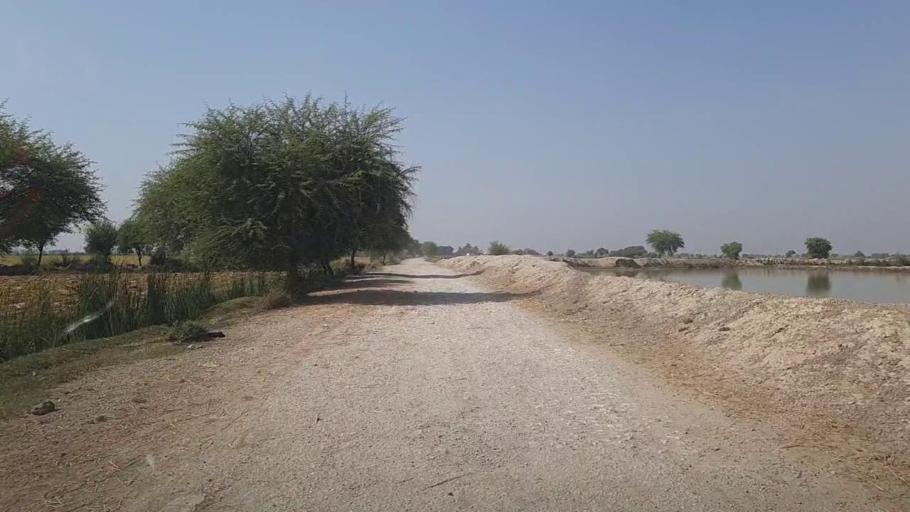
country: PK
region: Sindh
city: Kandhkot
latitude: 28.3934
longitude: 69.3008
